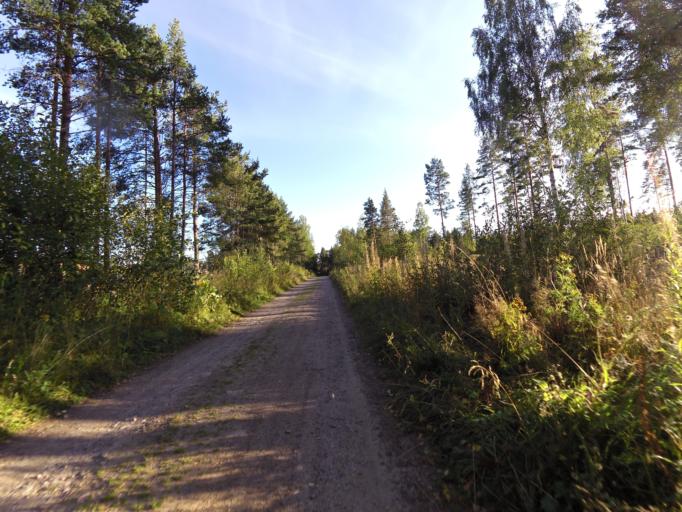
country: SE
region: Gaevleborg
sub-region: Gavle Kommun
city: Gavle
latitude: 60.6495
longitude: 17.1160
